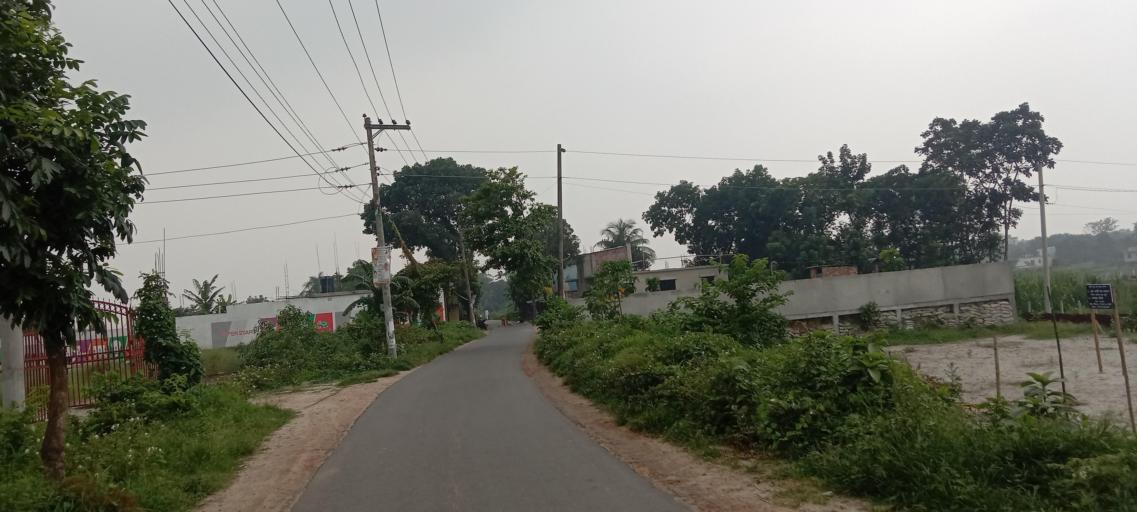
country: BD
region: Dhaka
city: Azimpur
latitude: 23.7387
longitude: 90.3177
